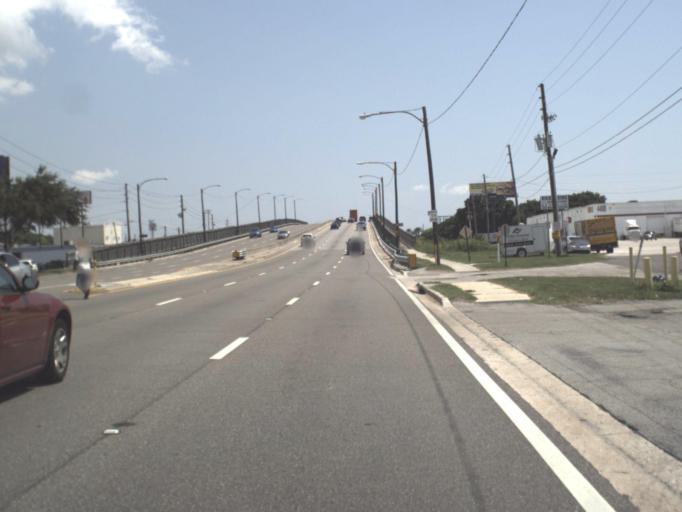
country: US
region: Florida
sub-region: Pinellas County
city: Lealman
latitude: 27.8128
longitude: -82.6796
